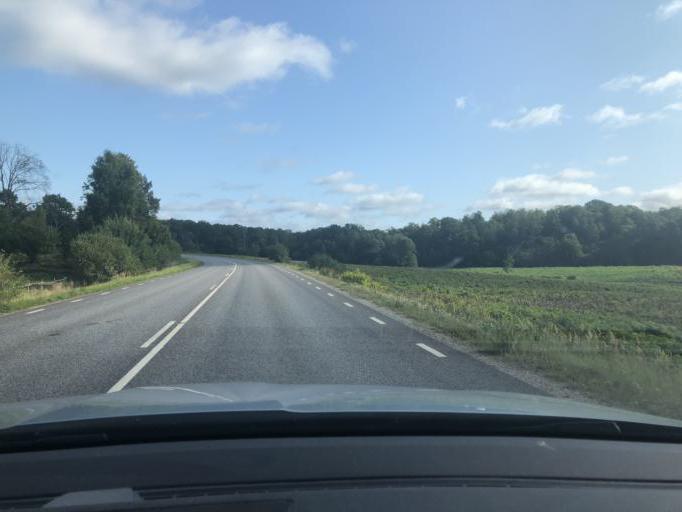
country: SE
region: Blekinge
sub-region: Olofstroms Kommun
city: Olofstroem
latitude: 56.2471
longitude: 14.5526
